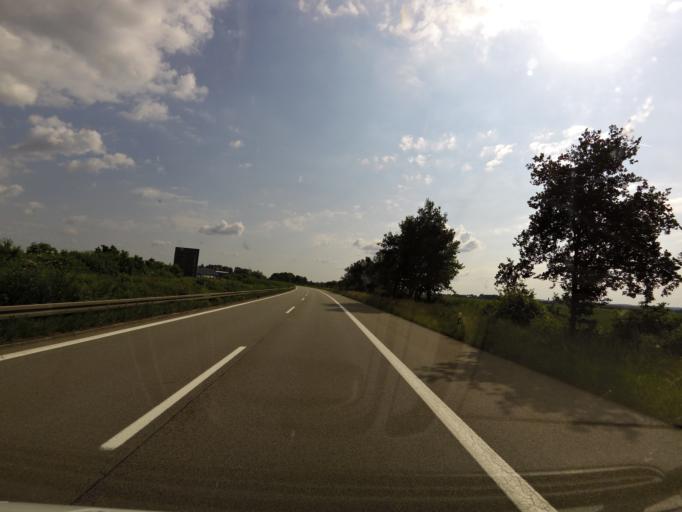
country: DE
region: Bavaria
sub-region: Lower Bavaria
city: Wallersdorf
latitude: 48.7425
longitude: 12.7373
